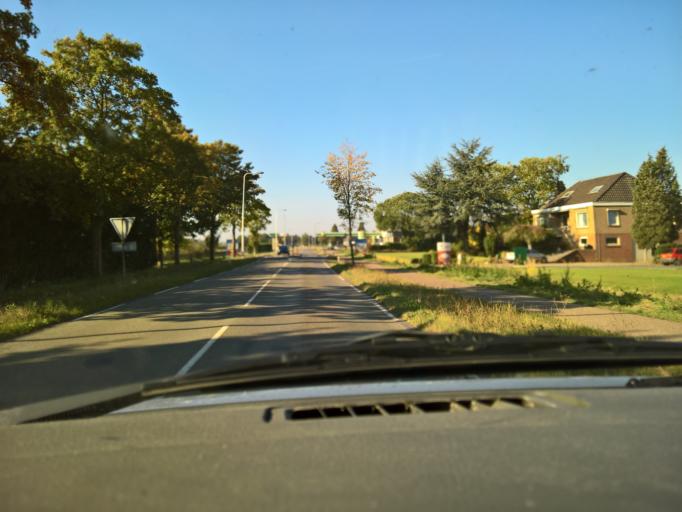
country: NL
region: Gelderland
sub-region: Gemeente Buren
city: Lienden
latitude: 51.8751
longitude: 5.5089
